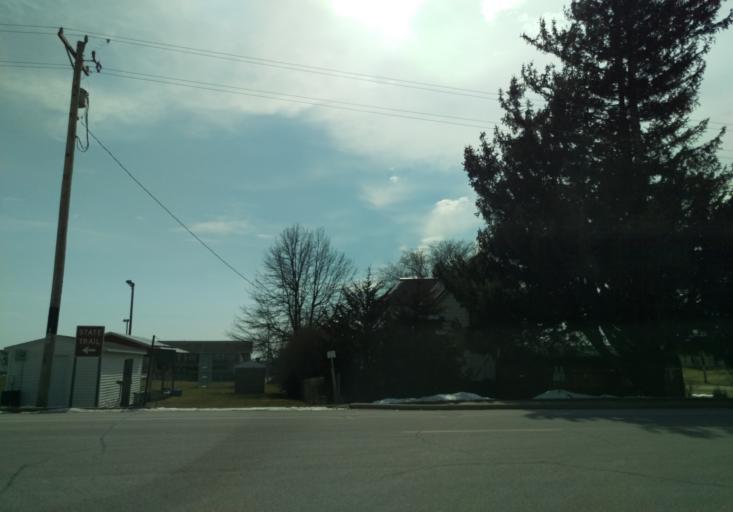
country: US
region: Minnesota
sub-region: Fillmore County
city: Preston
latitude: 43.7390
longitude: -92.1364
